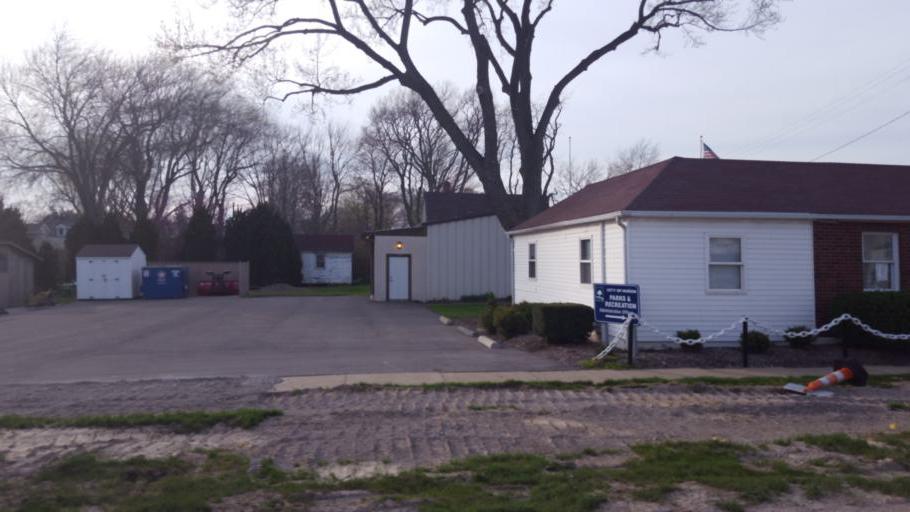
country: US
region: Ohio
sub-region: Erie County
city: Huron
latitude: 41.3968
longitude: -82.5521
